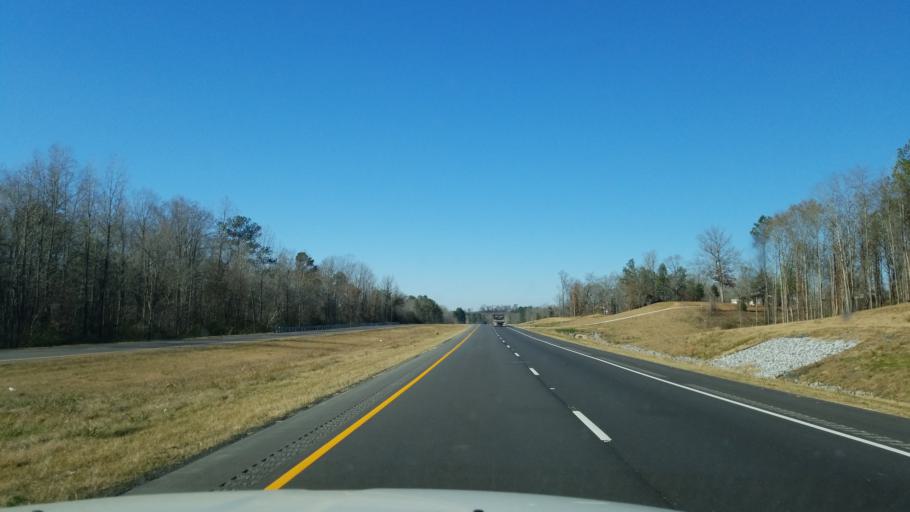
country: US
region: Alabama
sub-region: Pickens County
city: Reform
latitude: 33.3632
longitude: -87.9773
